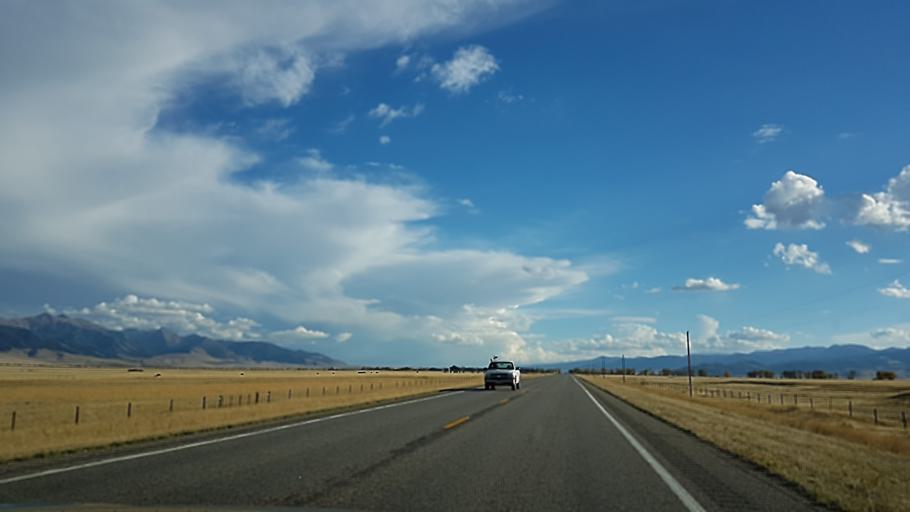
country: US
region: Montana
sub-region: Madison County
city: Virginia City
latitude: 45.2240
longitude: -111.6789
